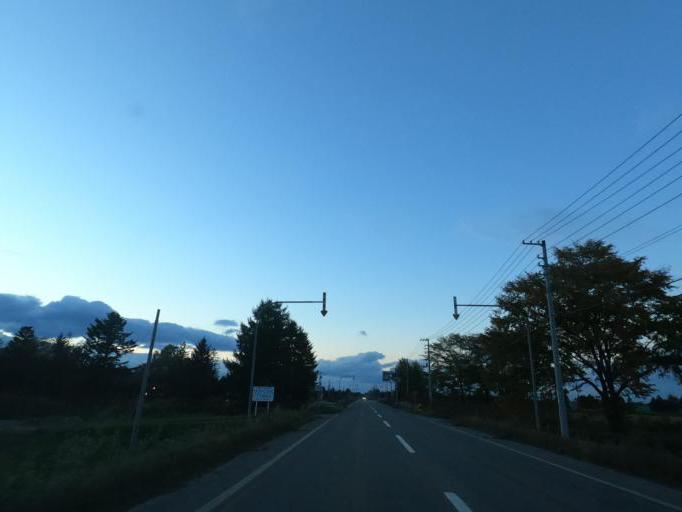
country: JP
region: Hokkaido
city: Obihiro
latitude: 42.6597
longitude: 143.1828
